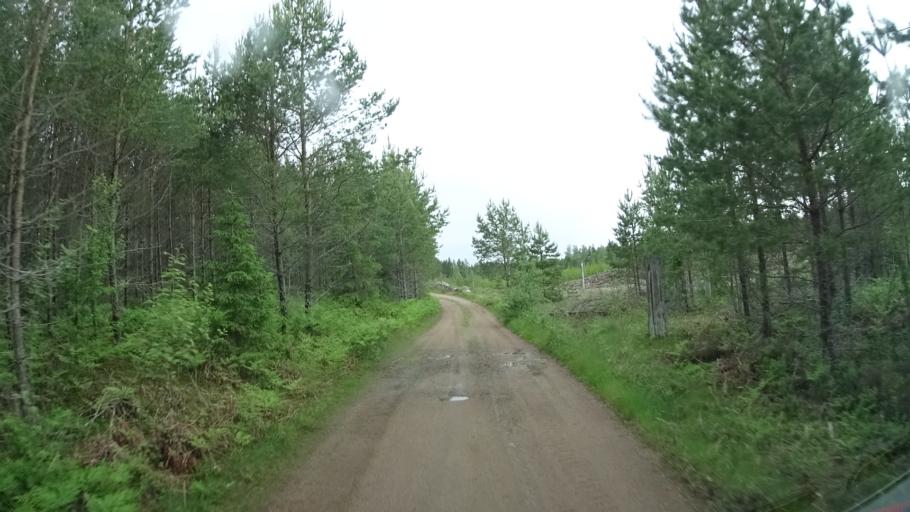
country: SE
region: Kalmar
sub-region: Vimmerby Kommun
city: Sodra Vi
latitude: 57.7143
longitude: 15.7832
